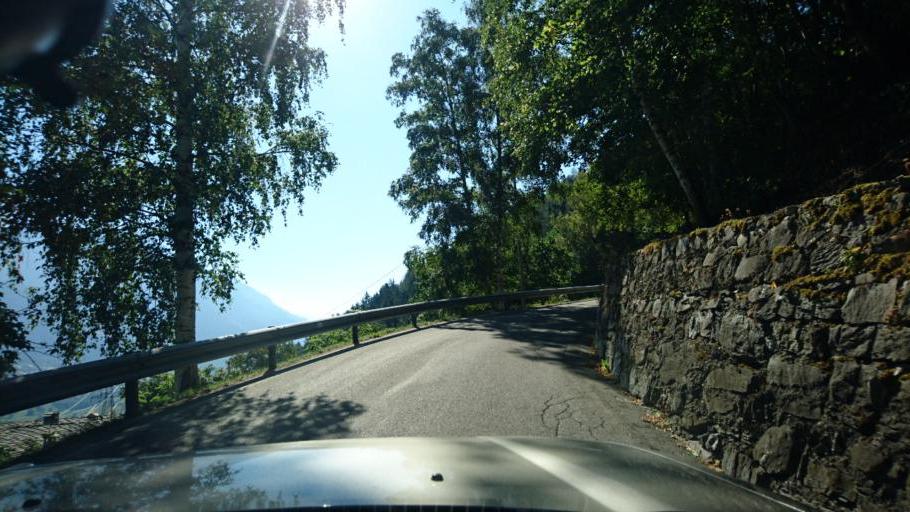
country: IT
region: Aosta Valley
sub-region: Valle d'Aosta
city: Morgex
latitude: 45.7490
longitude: 7.0395
